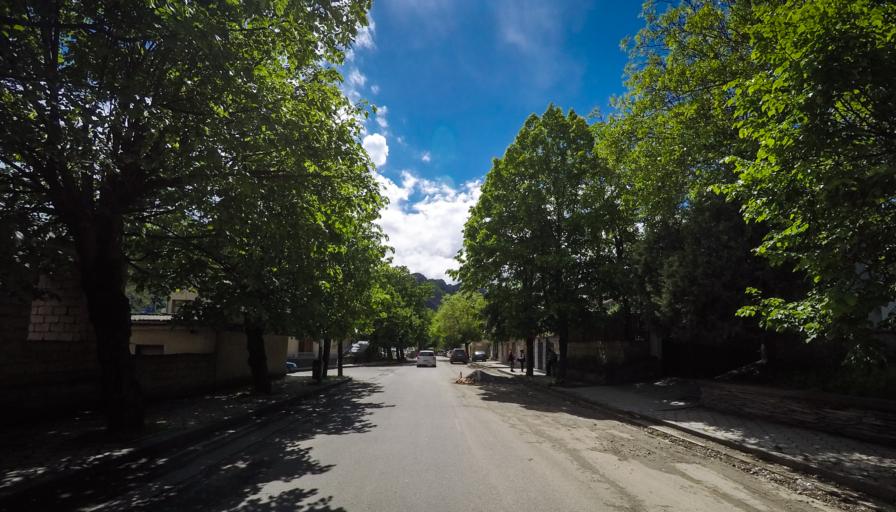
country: GE
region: Mtskheta-Mtianeti
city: Mtskheta
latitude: 41.8430
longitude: 44.7176
